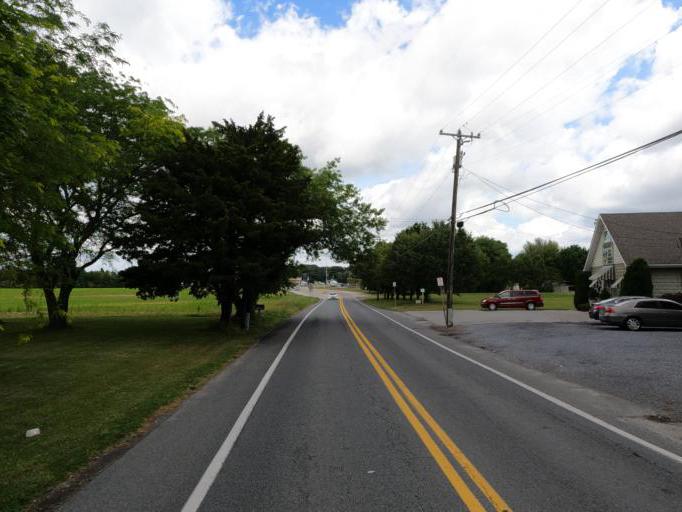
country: US
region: Delaware
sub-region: Sussex County
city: Lewes
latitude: 38.7244
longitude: -75.1308
